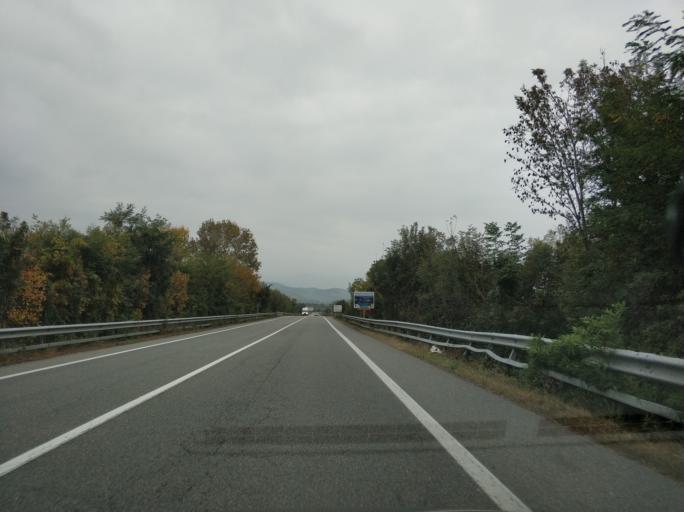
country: IT
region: Piedmont
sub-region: Provincia di Torino
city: Castellamonte
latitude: 45.3738
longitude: 7.7309
